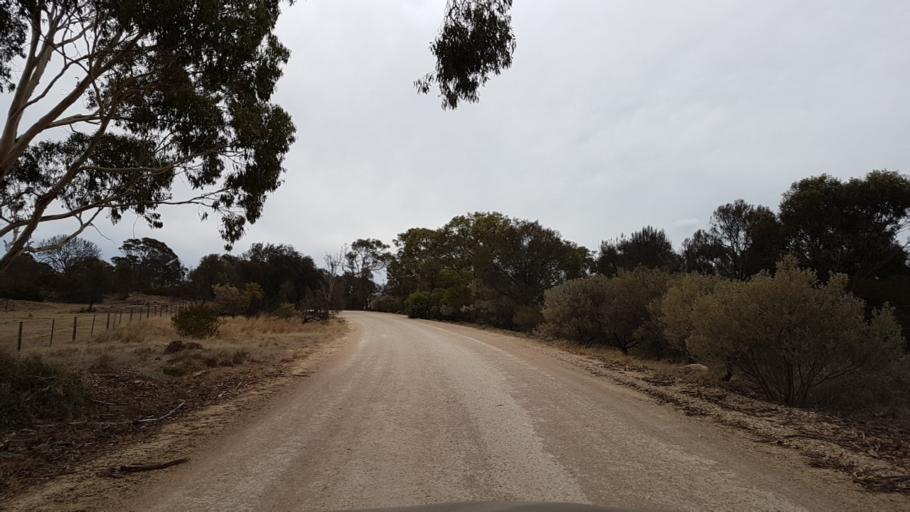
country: AU
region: South Australia
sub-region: Mount Barker
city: Callington
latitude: -35.0062
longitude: 139.0821
